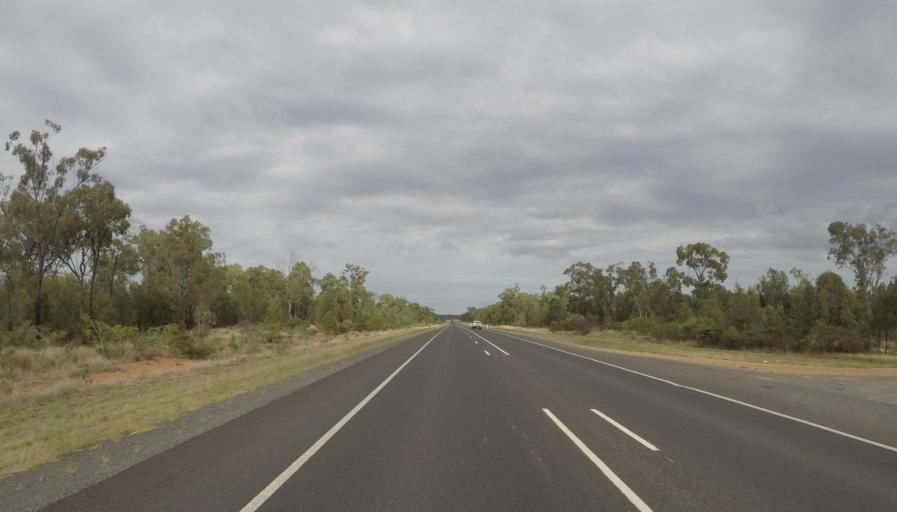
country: AU
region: Queensland
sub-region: Western Downs
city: Westcourt
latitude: -26.6598
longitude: 150.2168
